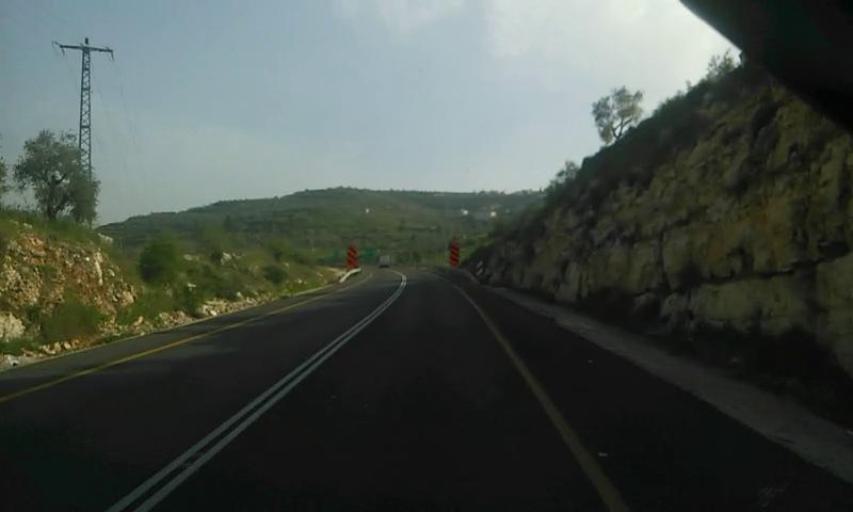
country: PS
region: West Bank
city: Jit
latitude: 32.2171
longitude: 35.1757
